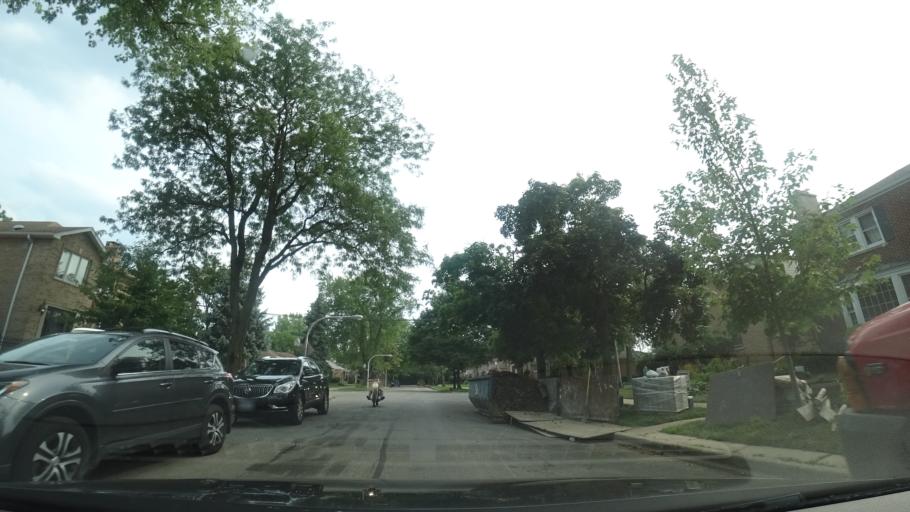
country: US
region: Illinois
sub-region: Cook County
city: Lincolnwood
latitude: 41.9944
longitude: -87.7300
